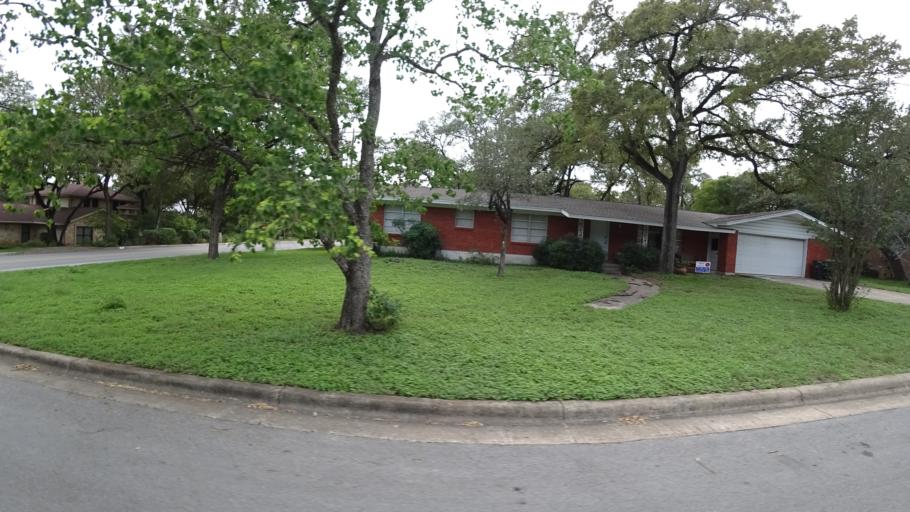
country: US
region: Texas
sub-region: Travis County
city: Rollingwood
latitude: 30.2755
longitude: -97.7924
